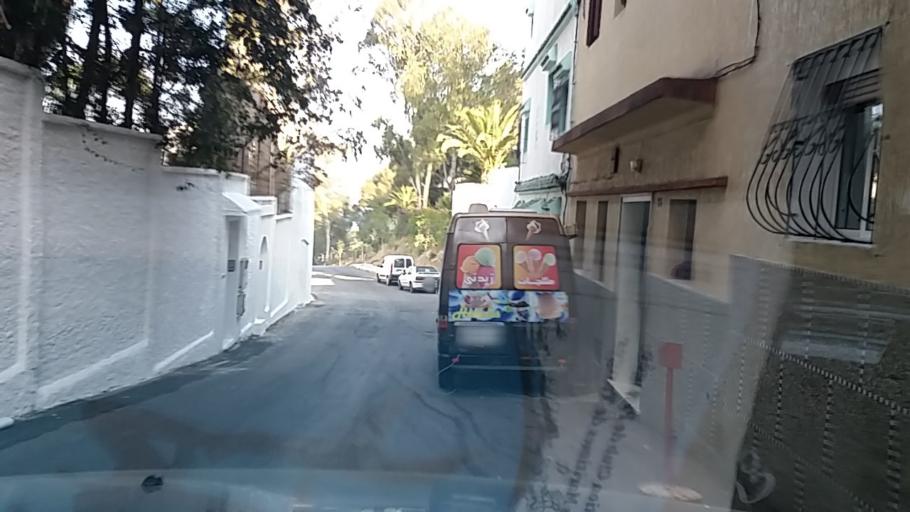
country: MA
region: Tanger-Tetouan
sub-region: Tanger-Assilah
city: Tangier
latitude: 35.7900
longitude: -5.8312
